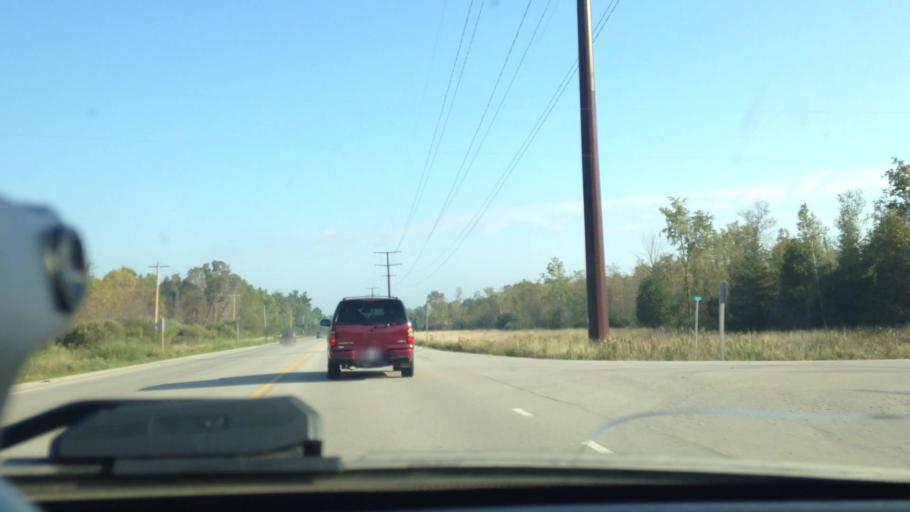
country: US
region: Wisconsin
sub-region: Marinette County
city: Peshtigo
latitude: 45.1806
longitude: -87.9957
